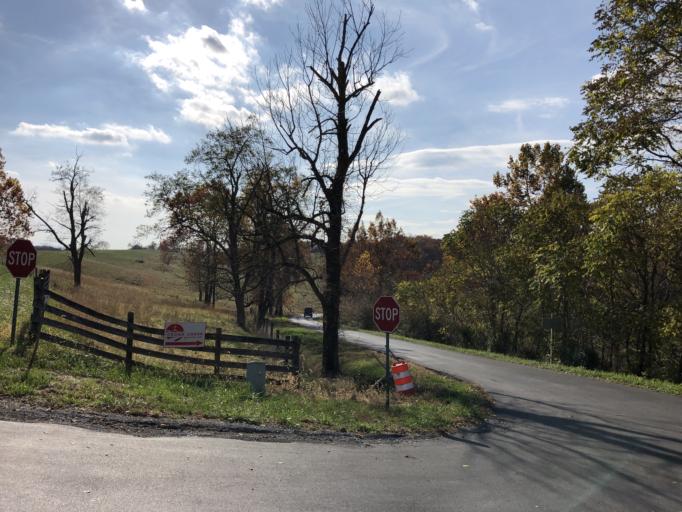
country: US
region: Virginia
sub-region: Frederick County
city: Middletown
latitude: 39.0959
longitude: -78.3223
